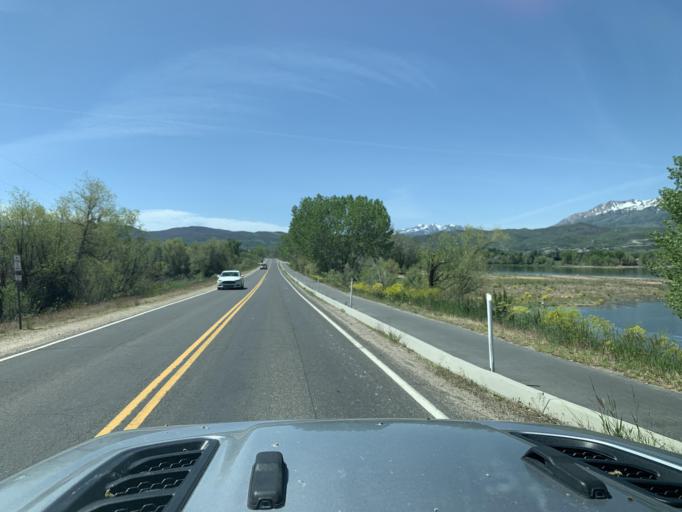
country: US
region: Utah
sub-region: Weber County
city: Wolf Creek
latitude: 41.2761
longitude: -111.7772
